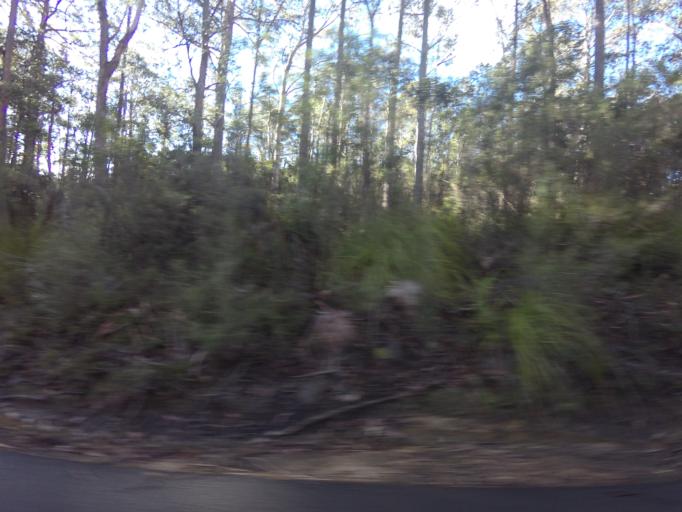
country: AU
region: Tasmania
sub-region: Glenorchy
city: Berriedale
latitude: -42.8417
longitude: 147.1654
